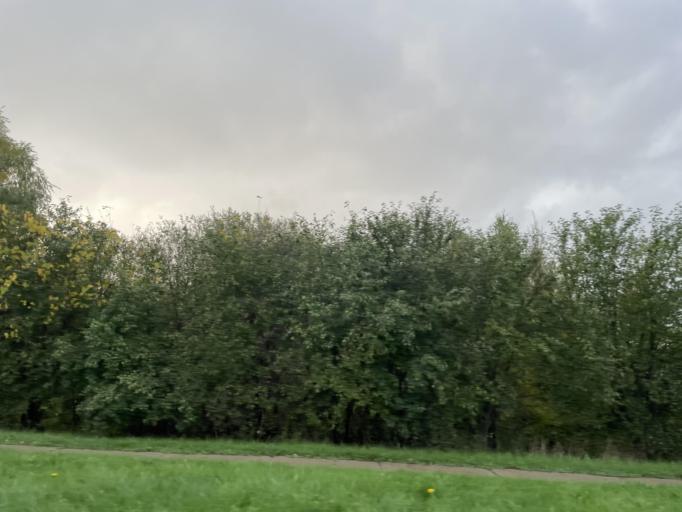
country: CA
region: Ontario
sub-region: Wellington County
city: Guelph
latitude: 43.5052
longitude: -80.2375
